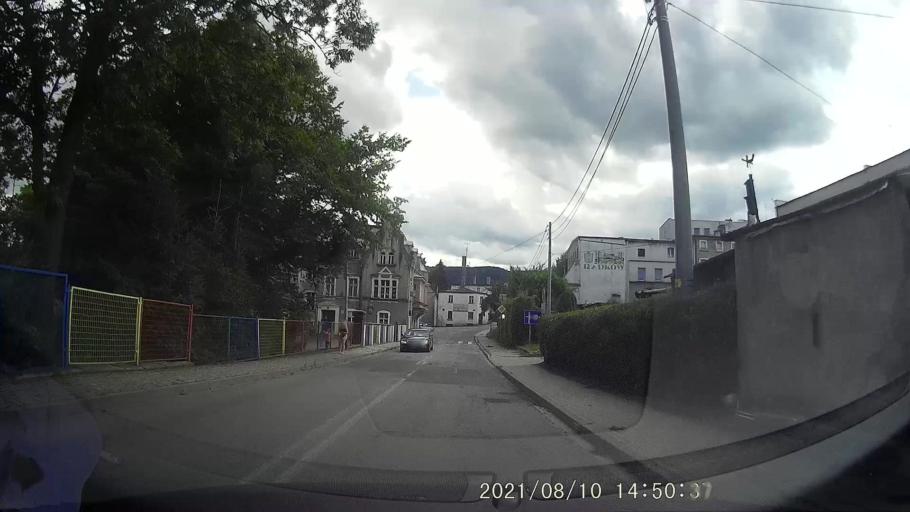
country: PL
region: Lower Silesian Voivodeship
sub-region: Powiat klodzki
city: Radkow
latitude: 50.5044
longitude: 16.4033
